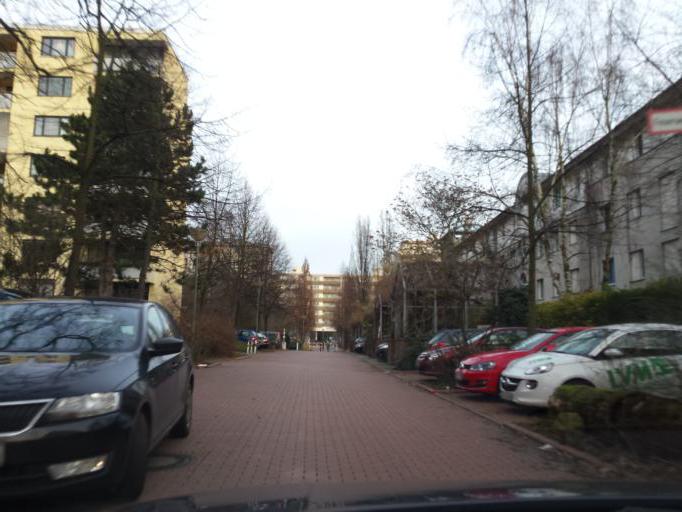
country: DE
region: Berlin
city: Dahlem
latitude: 52.4388
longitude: 13.2768
